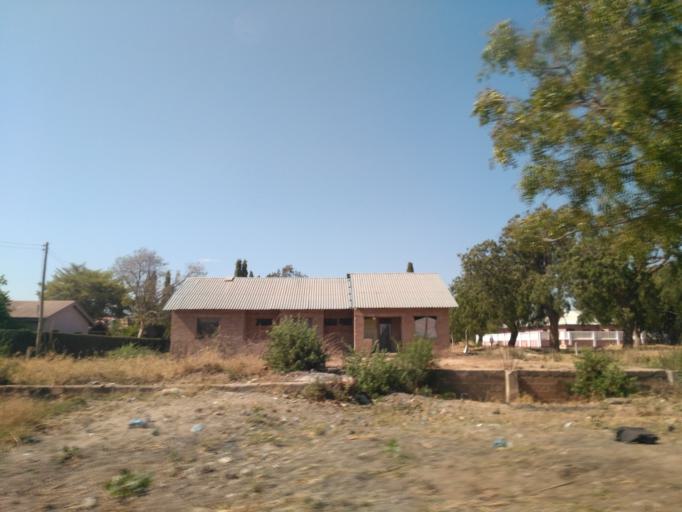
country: TZ
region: Dodoma
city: Dodoma
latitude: -6.1628
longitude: 35.7527
